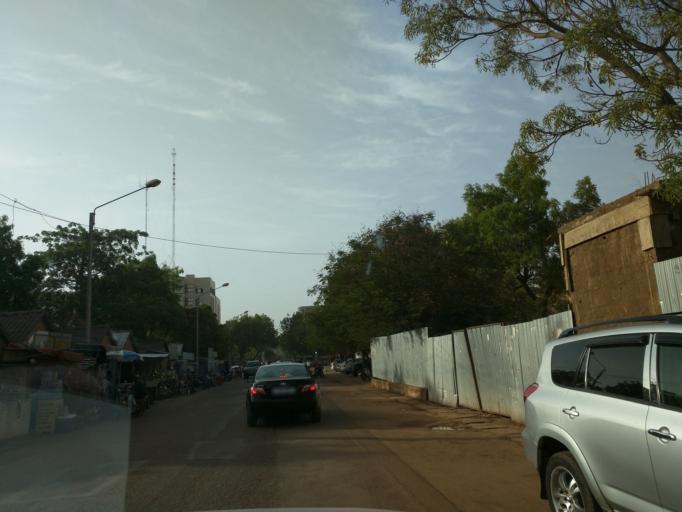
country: BF
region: Centre
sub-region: Kadiogo Province
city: Ouagadougou
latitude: 12.3711
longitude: -1.5160
